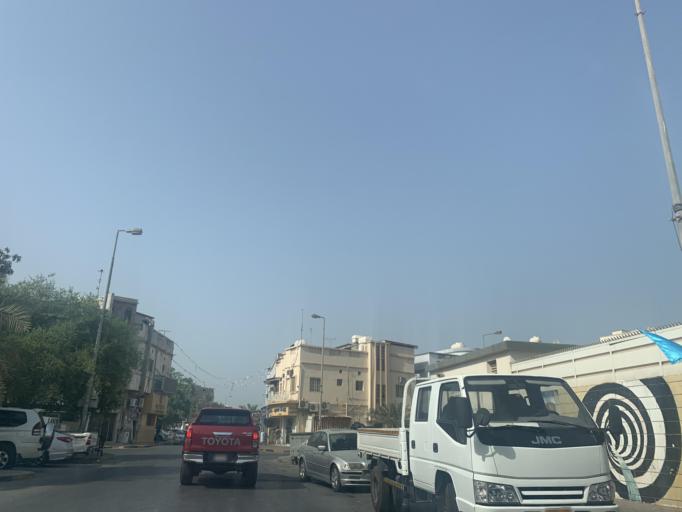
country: BH
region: Manama
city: Jidd Hafs
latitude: 26.2130
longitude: 50.4583
